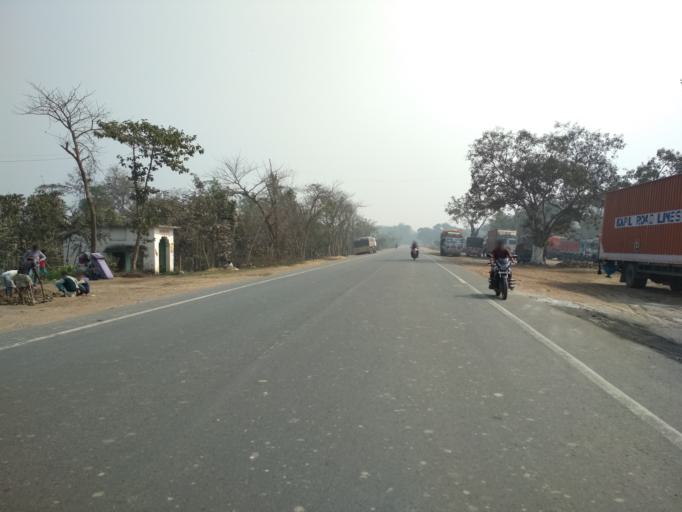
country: IN
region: Bihar
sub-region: Khagaria
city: Khagaria
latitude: 25.5070
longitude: 86.5839
